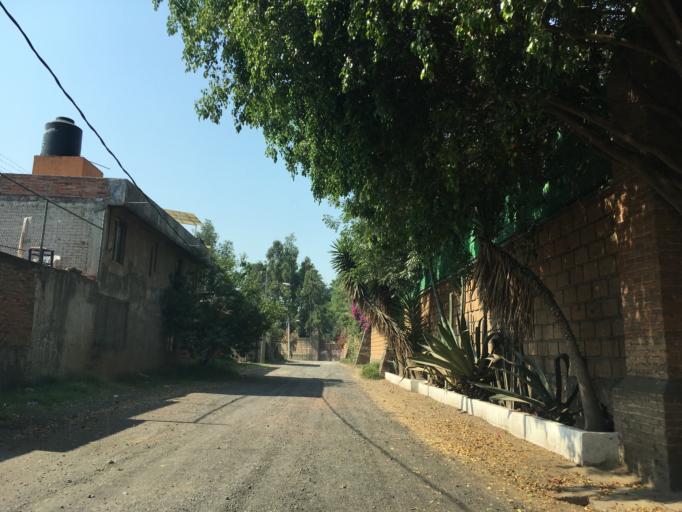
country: MX
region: Michoacan
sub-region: Morelia
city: Morelos
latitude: 19.6714
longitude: -101.2233
